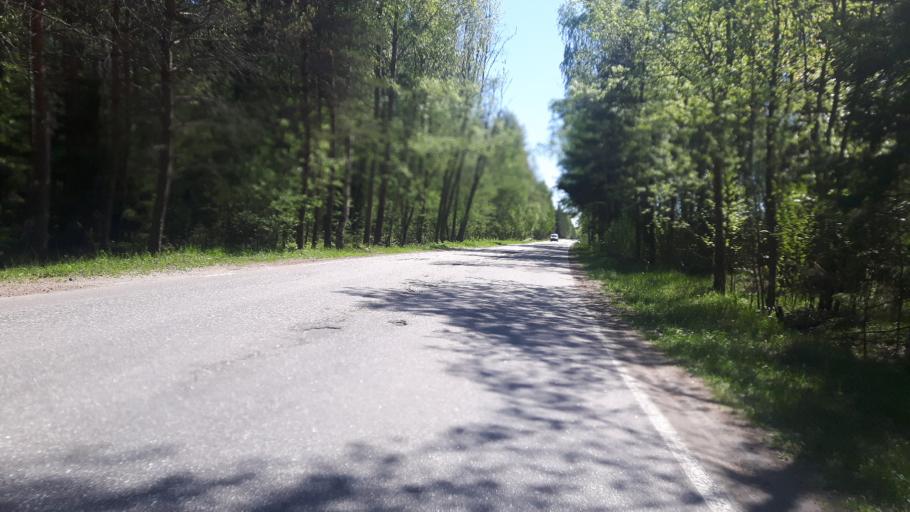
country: RU
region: Leningrad
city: Glebychevo
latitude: 60.3573
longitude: 28.8120
